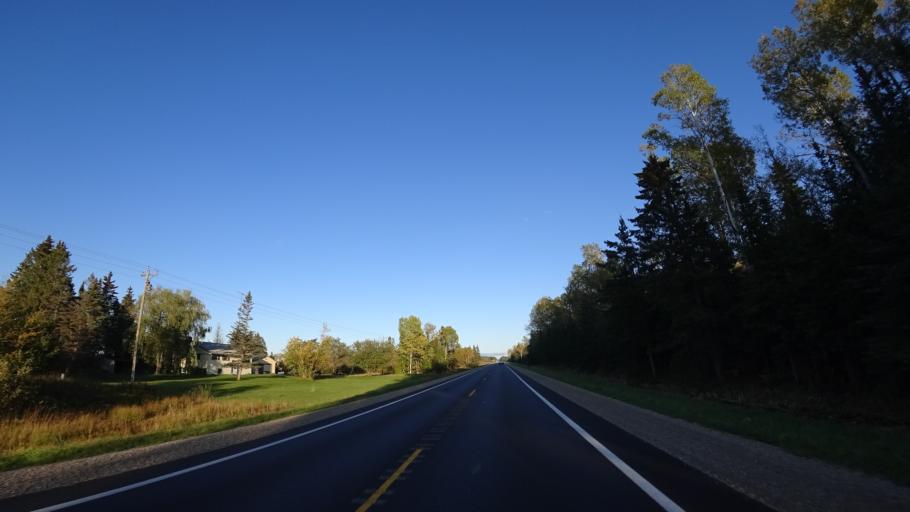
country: US
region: Michigan
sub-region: Luce County
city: Newberry
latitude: 46.3105
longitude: -85.5876
